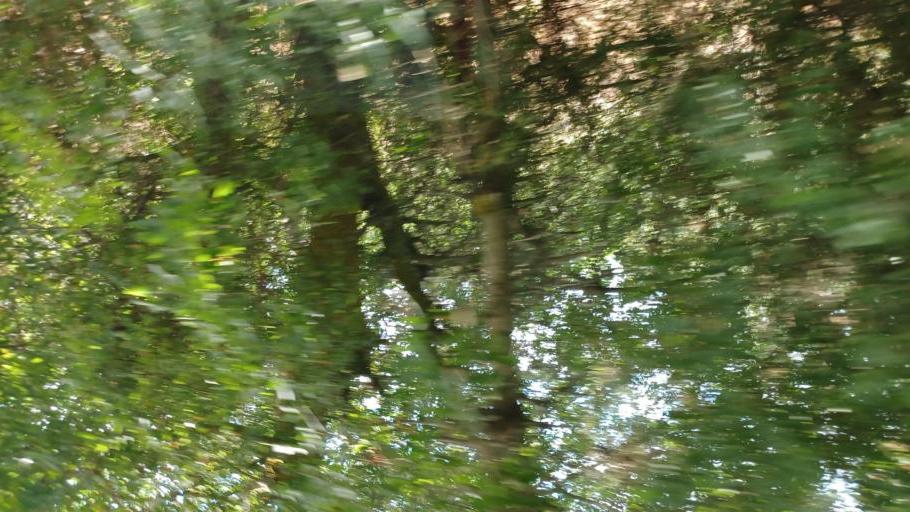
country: CY
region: Pafos
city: Tala
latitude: 34.8610
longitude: 32.4563
